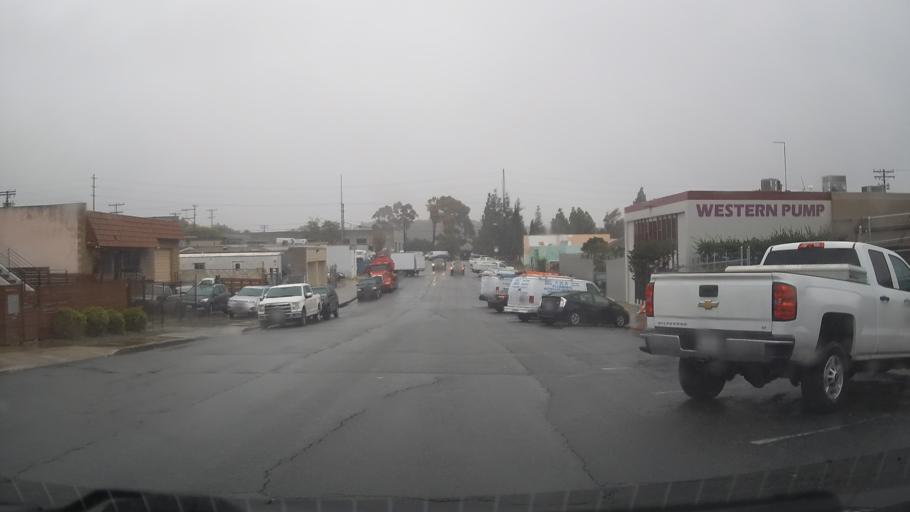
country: US
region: California
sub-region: San Diego County
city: San Diego
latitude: 32.7138
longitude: -117.1250
